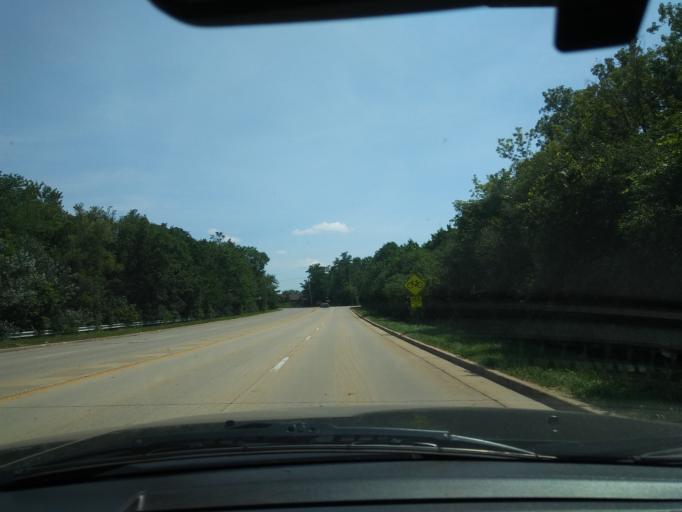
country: US
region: Illinois
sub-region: Cook County
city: Oak Forest
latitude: 41.6261
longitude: -87.7764
